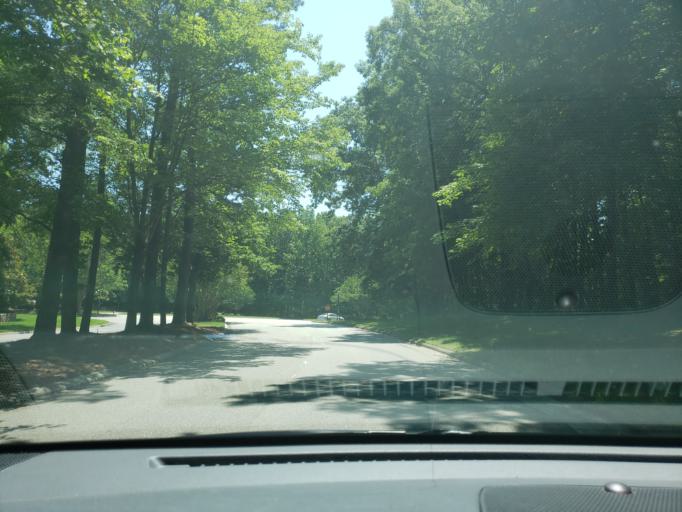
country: US
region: North Carolina
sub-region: Durham County
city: Gorman
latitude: 36.1290
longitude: -78.8649
